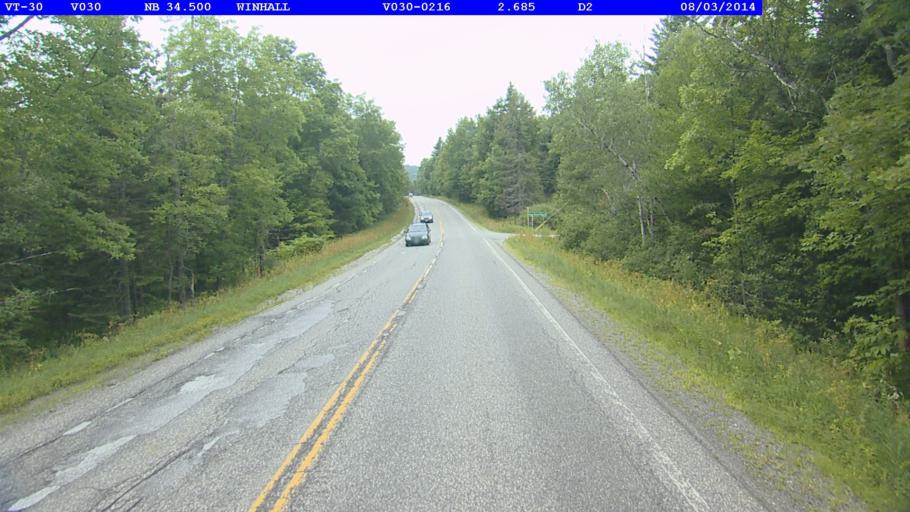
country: US
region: Vermont
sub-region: Bennington County
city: Manchester Center
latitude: 43.1551
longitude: -72.9143
